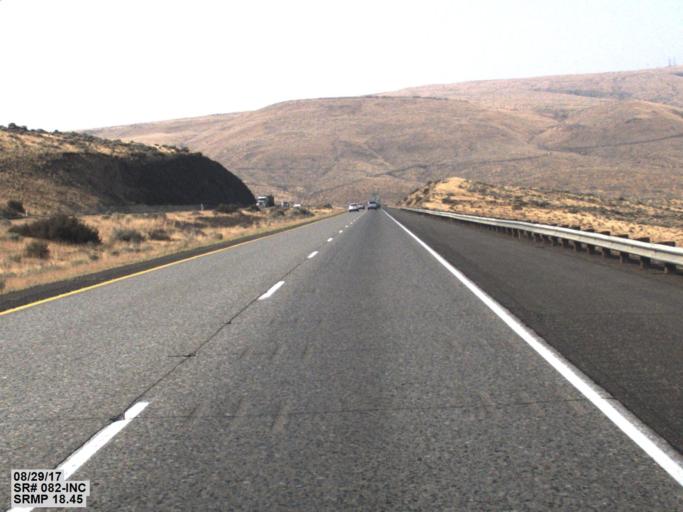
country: US
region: Washington
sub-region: Yakima County
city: Terrace Heights
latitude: 46.7563
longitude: -120.3833
